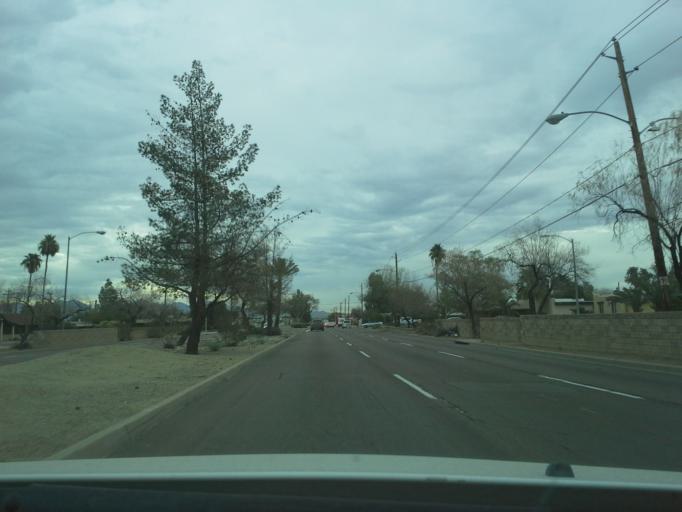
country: US
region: Arizona
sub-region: Maricopa County
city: Paradise Valley
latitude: 33.5969
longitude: -112.0191
